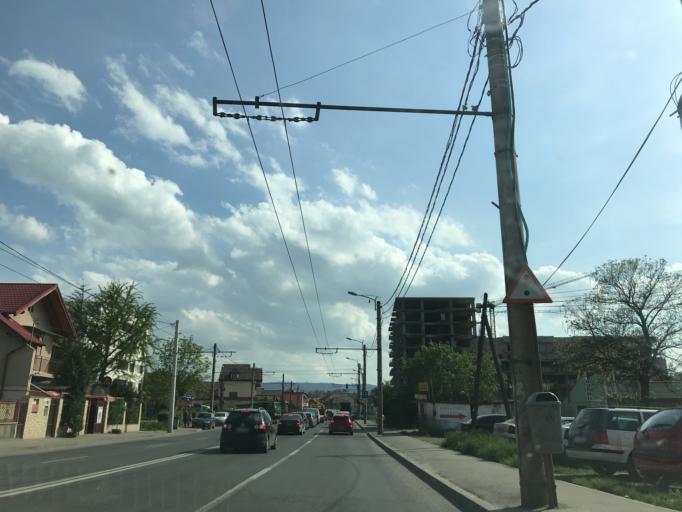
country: RO
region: Cluj
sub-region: Municipiul Cluj-Napoca
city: Cluj-Napoca
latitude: 46.7898
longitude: 23.6157
